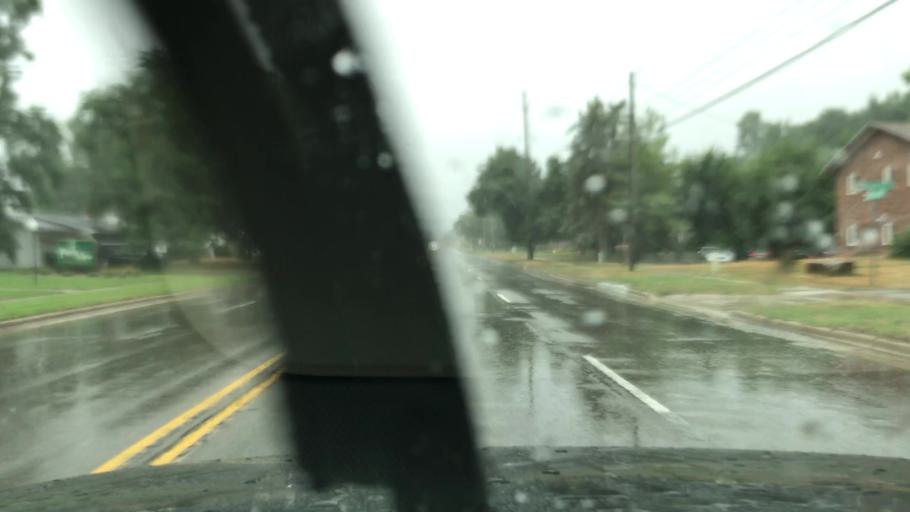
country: US
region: Michigan
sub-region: Kent County
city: Wyoming
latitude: 42.9049
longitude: -85.7247
